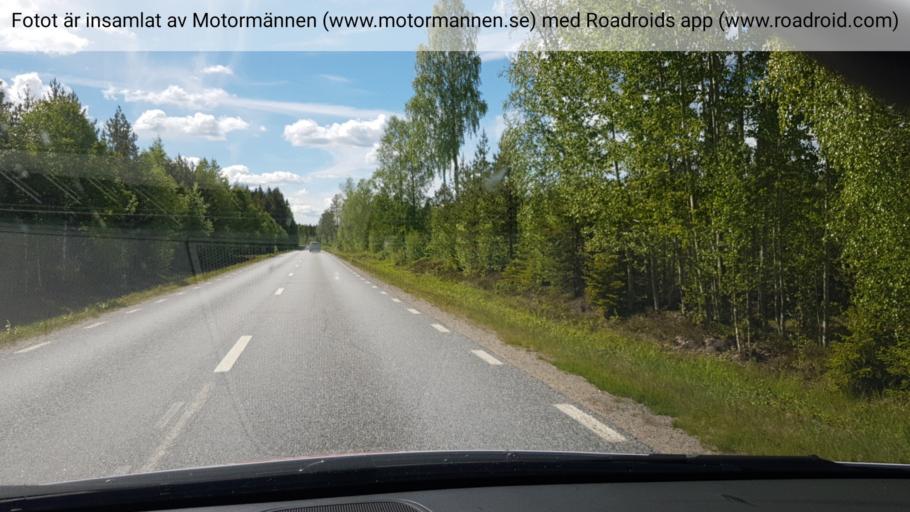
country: SE
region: Vaesterbotten
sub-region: Skelleftea Kommun
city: Burtraesk
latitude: 64.5142
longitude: 20.6047
